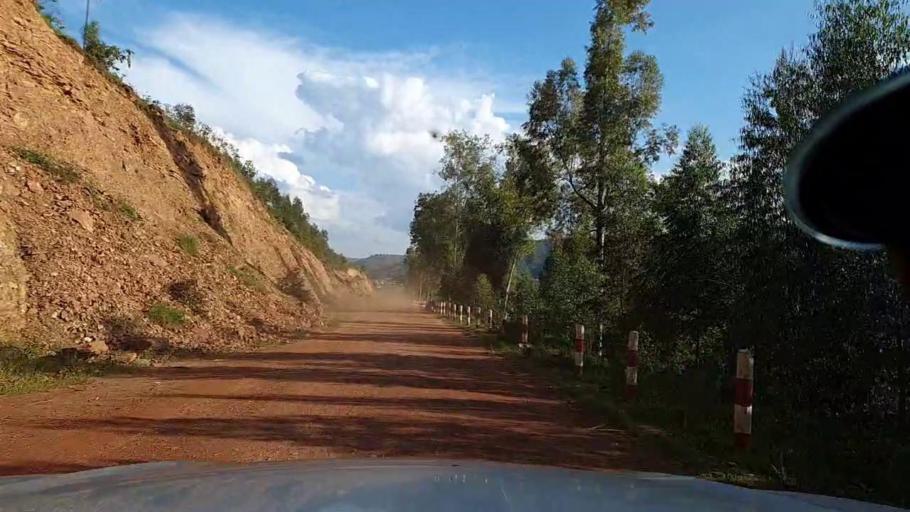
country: RW
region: Kigali
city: Kigali
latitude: -1.8710
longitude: 29.9319
